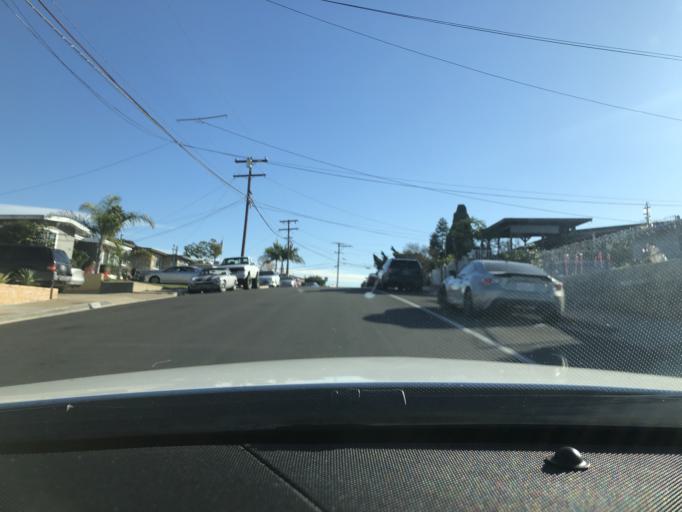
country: US
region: California
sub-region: San Diego County
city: Lemon Grove
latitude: 32.7487
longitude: -117.0640
